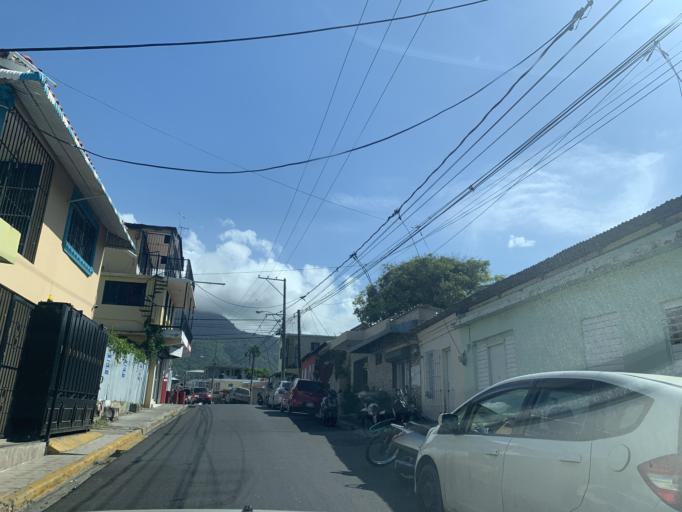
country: DO
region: Puerto Plata
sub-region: Puerto Plata
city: Puerto Plata
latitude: 19.7957
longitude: -70.6933
